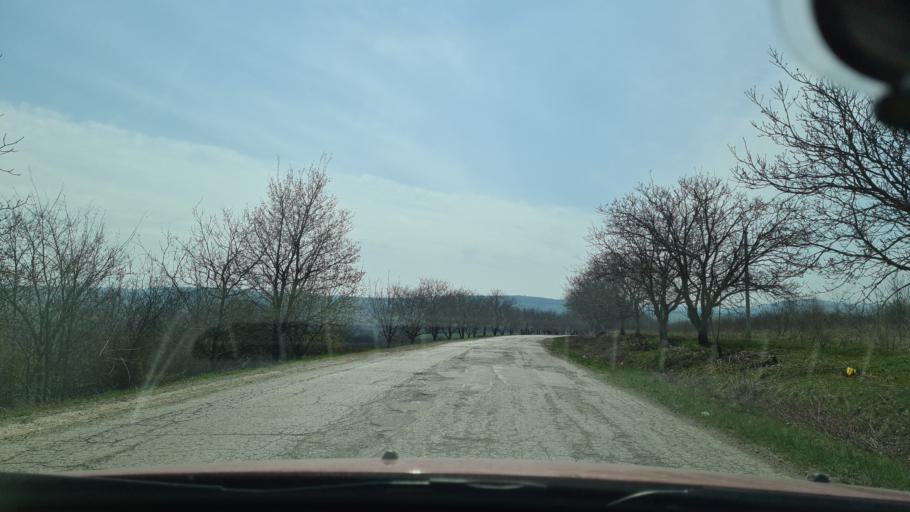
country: MD
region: Ungheni
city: Ungheni
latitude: 47.2883
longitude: 27.9212
